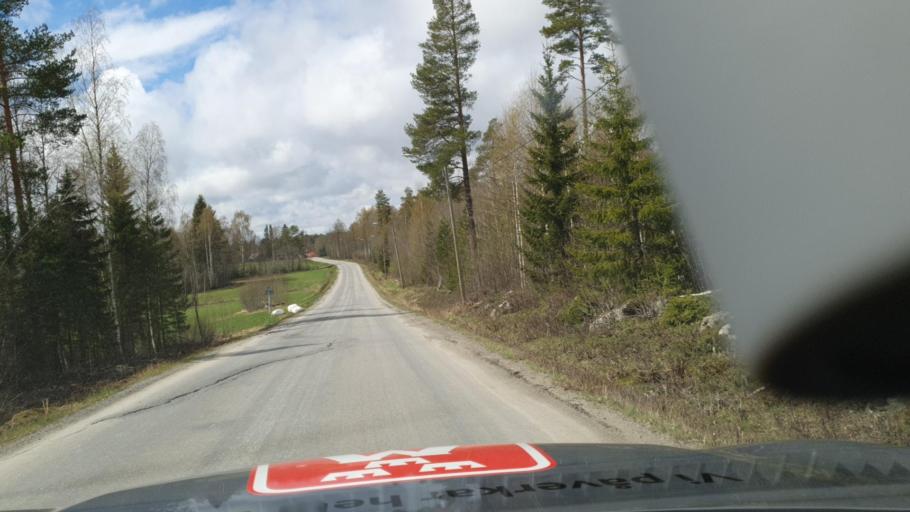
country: SE
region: Vaesterbotten
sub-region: Bjurholms Kommun
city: Bjurholm
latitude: 63.6957
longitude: 18.8887
